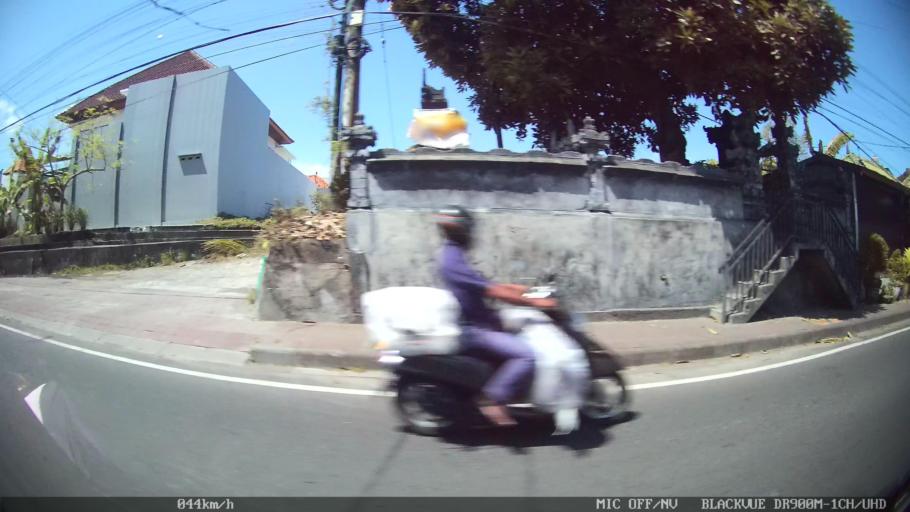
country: ID
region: Bali
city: Denpasar
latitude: -8.6585
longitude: 115.1750
